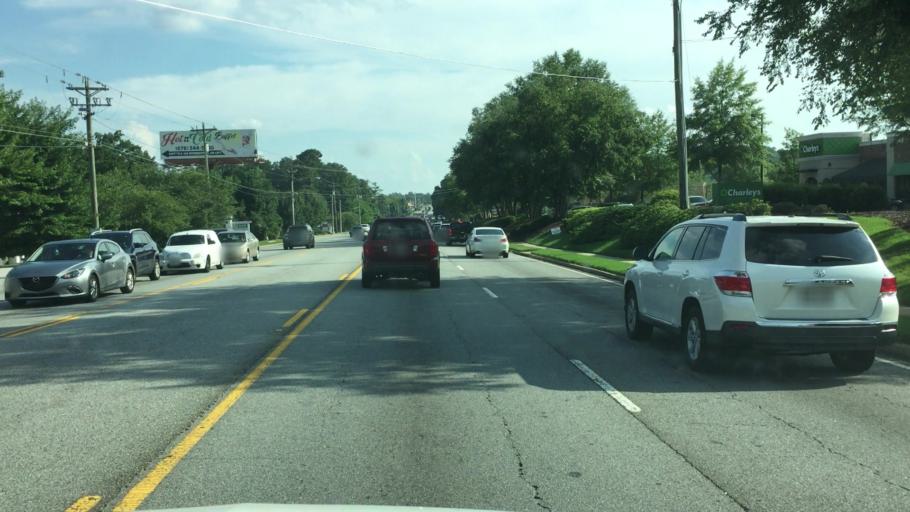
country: US
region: Georgia
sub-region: Gwinnett County
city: Snellville
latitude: 33.8676
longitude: -84.0160
